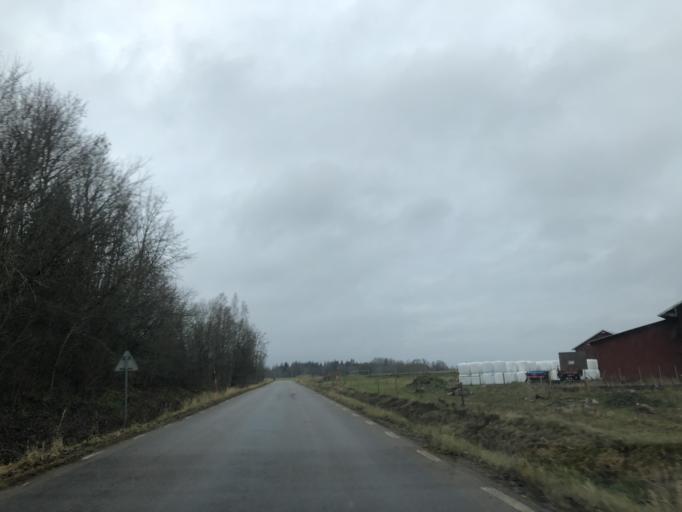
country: SE
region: Vaestra Goetaland
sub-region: Ulricehamns Kommun
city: Ulricehamn
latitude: 57.8831
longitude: 13.5145
